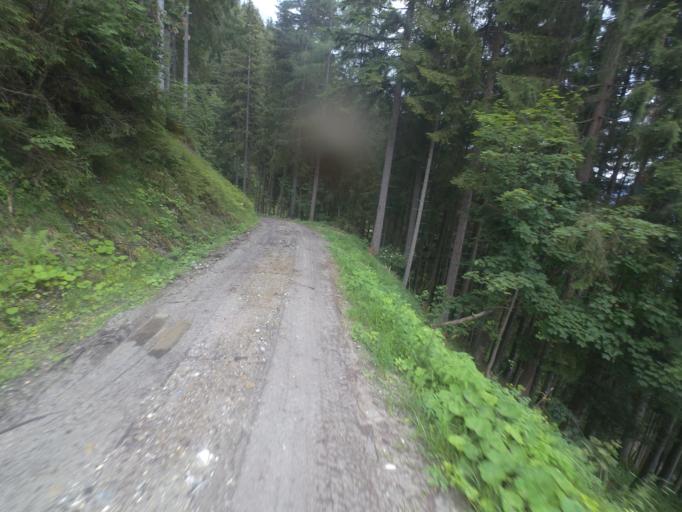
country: AT
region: Salzburg
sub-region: Politischer Bezirk Sankt Johann im Pongau
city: Schwarzach im Pongau
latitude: 47.3096
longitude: 13.1587
